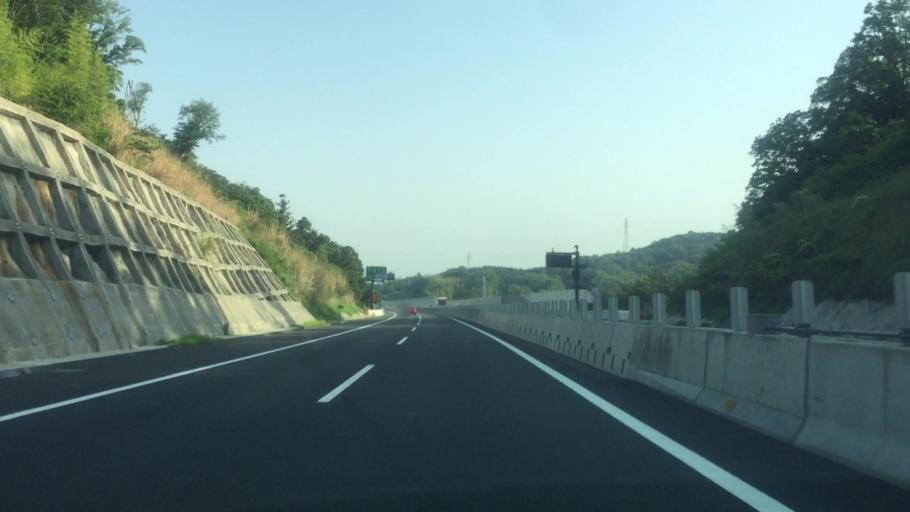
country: JP
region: Aichi
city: Okazaki
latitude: 35.0217
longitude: 137.2259
